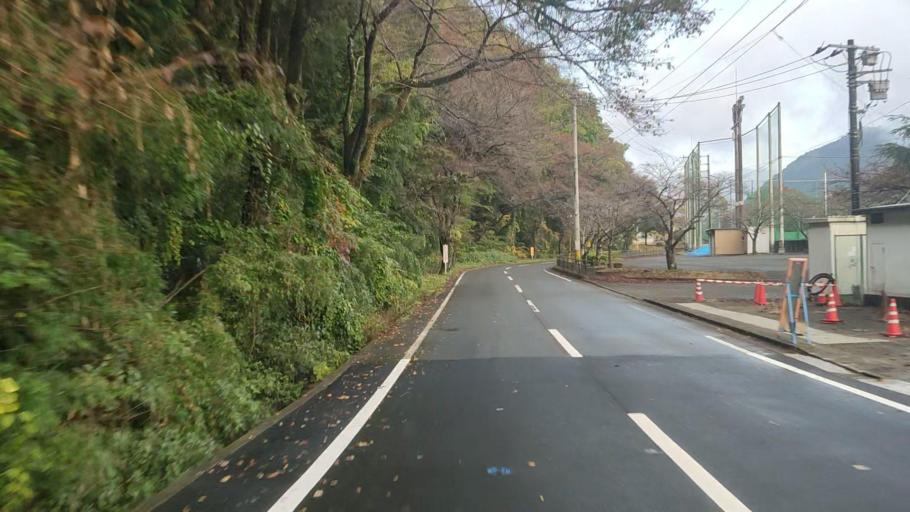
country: JP
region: Shizuoka
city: Fujinomiya
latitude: 35.2766
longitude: 138.4572
